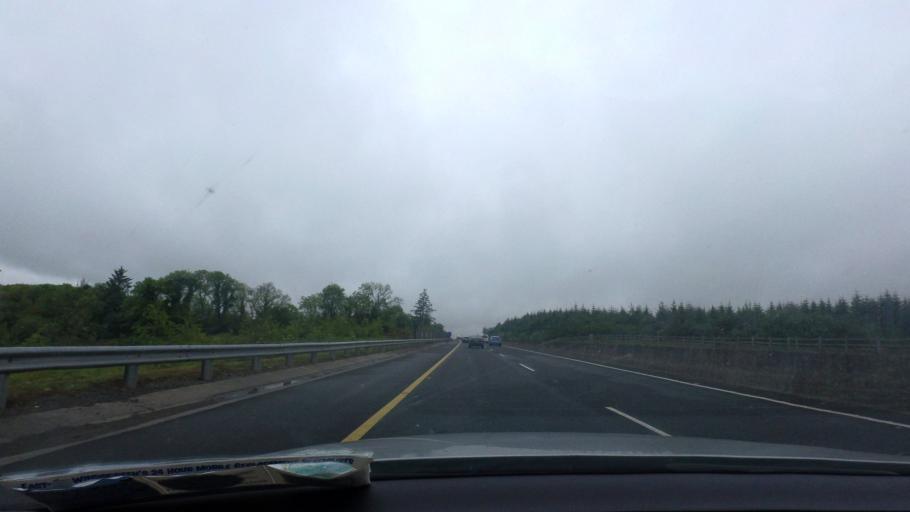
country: IE
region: Munster
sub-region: North Tipperary
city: Newport
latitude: 52.7528
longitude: -8.4190
